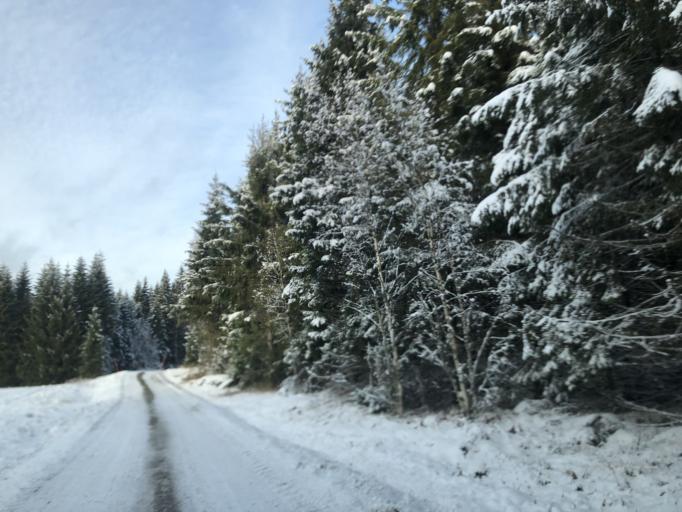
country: SE
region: Vaestra Goetaland
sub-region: Ulricehamns Kommun
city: Ulricehamn
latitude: 57.7477
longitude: 13.5077
